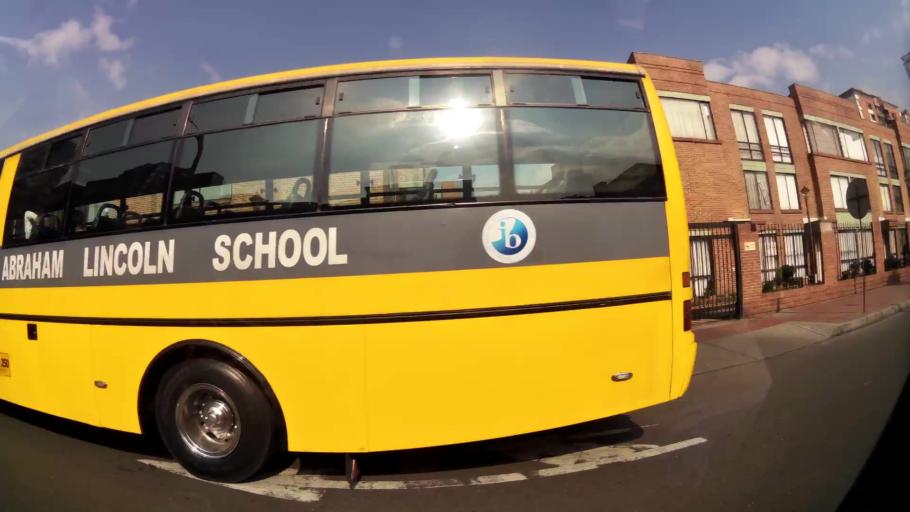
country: CO
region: Bogota D.C.
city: Barrio San Luis
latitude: 4.7383
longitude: -74.0597
